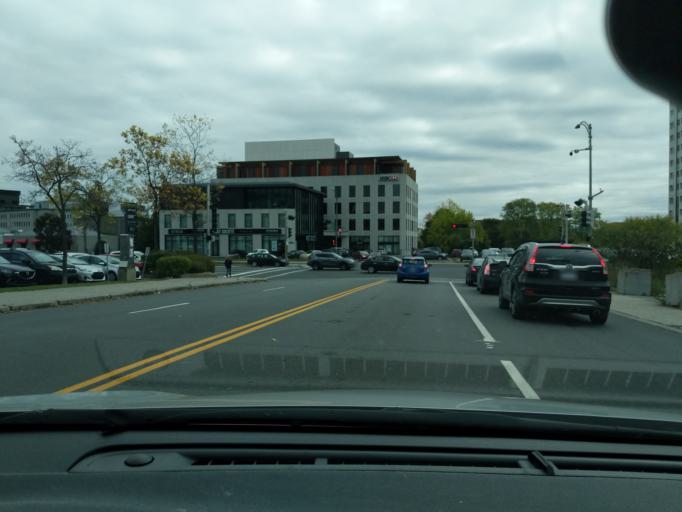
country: CA
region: Quebec
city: L'Ancienne-Lorette
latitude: 46.7687
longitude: -71.2868
